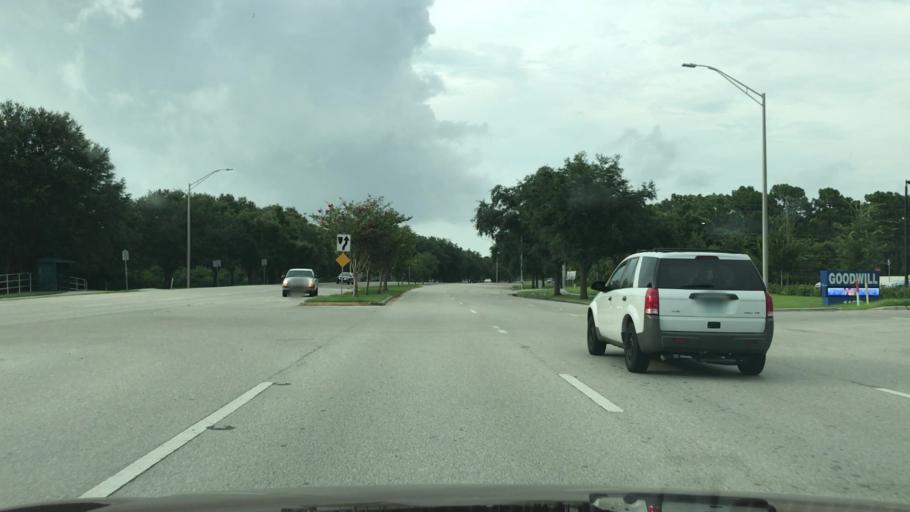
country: US
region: Florida
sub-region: Sarasota County
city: Venice Gardens
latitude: 27.0808
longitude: -82.3888
